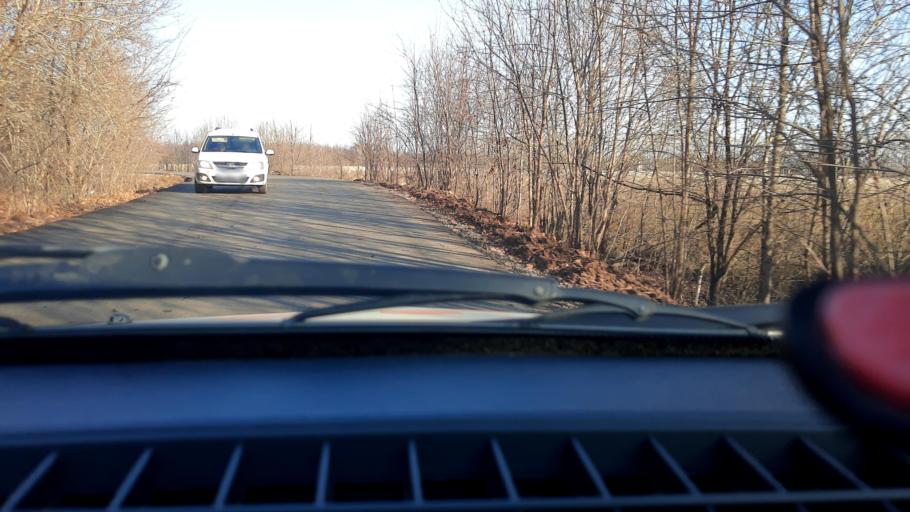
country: RU
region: Bashkortostan
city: Kabakovo
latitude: 54.6172
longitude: 56.1525
